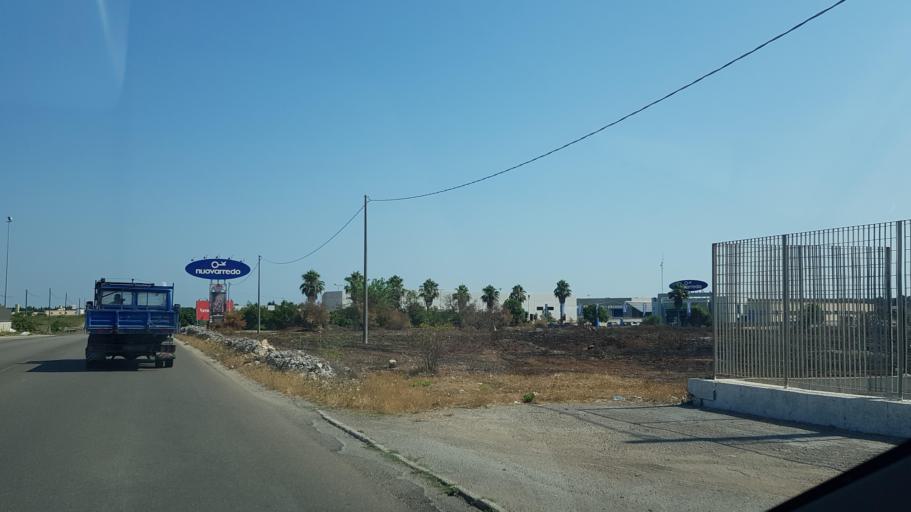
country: IT
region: Apulia
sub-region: Provincia di Lecce
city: Nociglia
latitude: 40.0132
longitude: 18.3242
